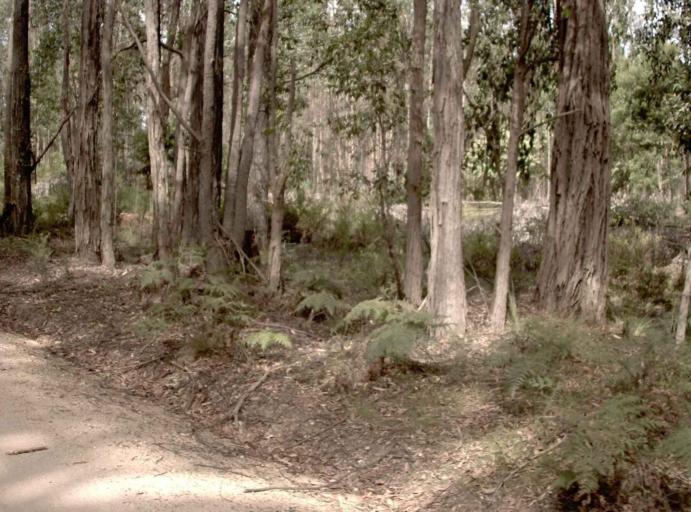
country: AU
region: Victoria
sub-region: East Gippsland
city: Lakes Entrance
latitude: -37.6322
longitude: 148.6751
